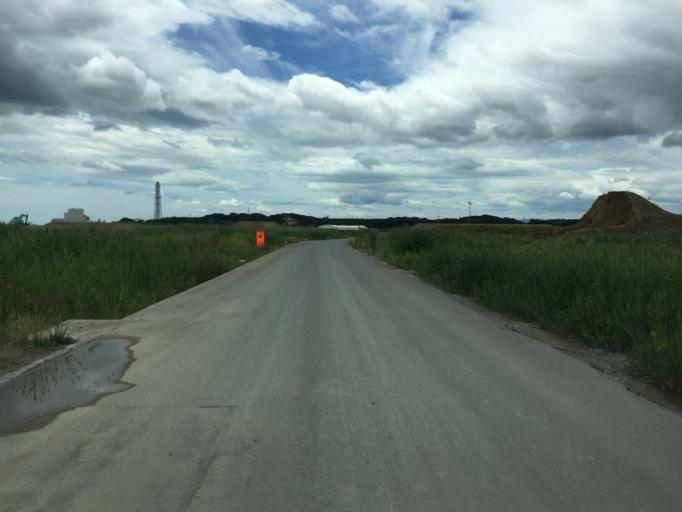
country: JP
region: Fukushima
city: Namie
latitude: 37.6908
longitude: 141.0095
